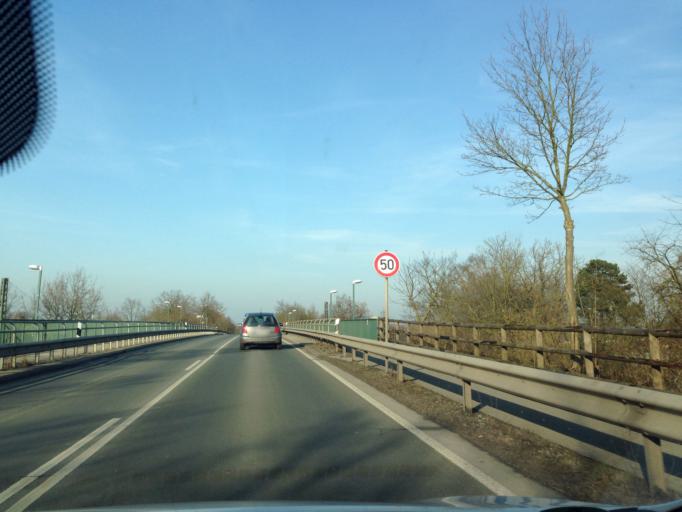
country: DE
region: North Rhine-Westphalia
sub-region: Regierungsbezirk Munster
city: Muenster
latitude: 51.9781
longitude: 7.6596
